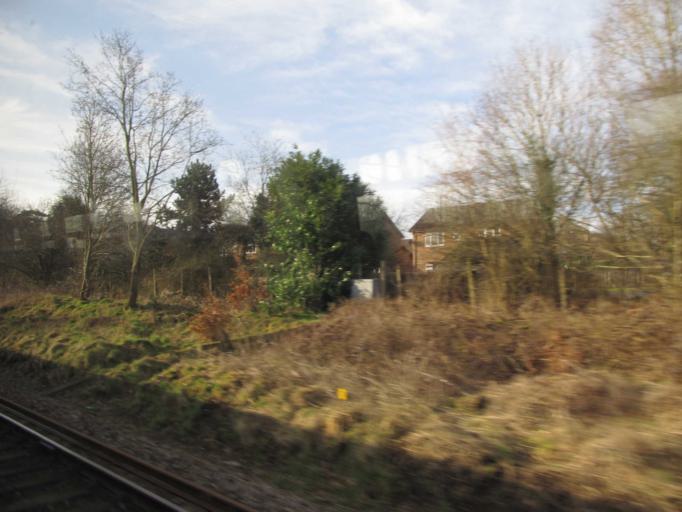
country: GB
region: England
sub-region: Surrey
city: Frimley
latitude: 51.3247
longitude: -0.7700
